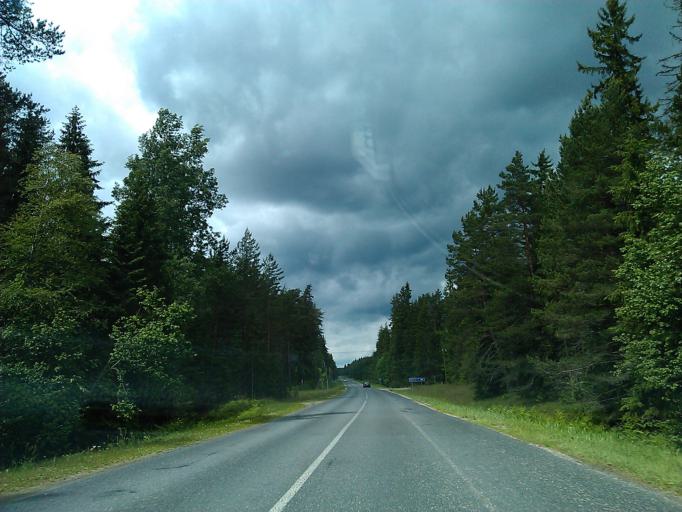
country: LV
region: Talsu Rajons
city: Stende
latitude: 57.0860
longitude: 22.4188
